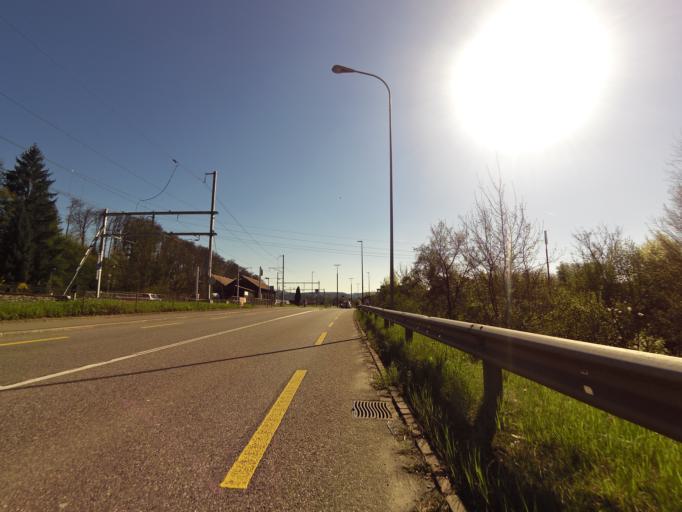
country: CH
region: Aargau
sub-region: Bezirk Zurzach
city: Koblenz
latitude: 47.6041
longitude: 8.2294
